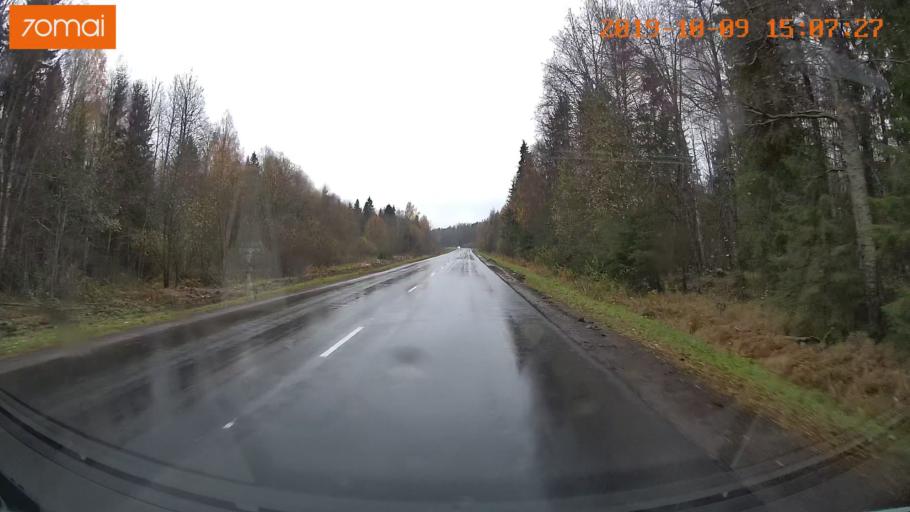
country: RU
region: Kostroma
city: Susanino
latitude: 58.2190
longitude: 41.6501
